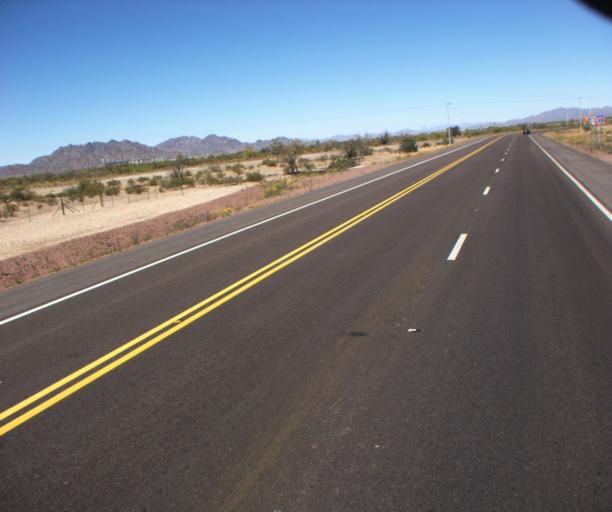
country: US
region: Arizona
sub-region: Maricopa County
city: Gila Bend
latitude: 32.9547
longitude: -112.6849
